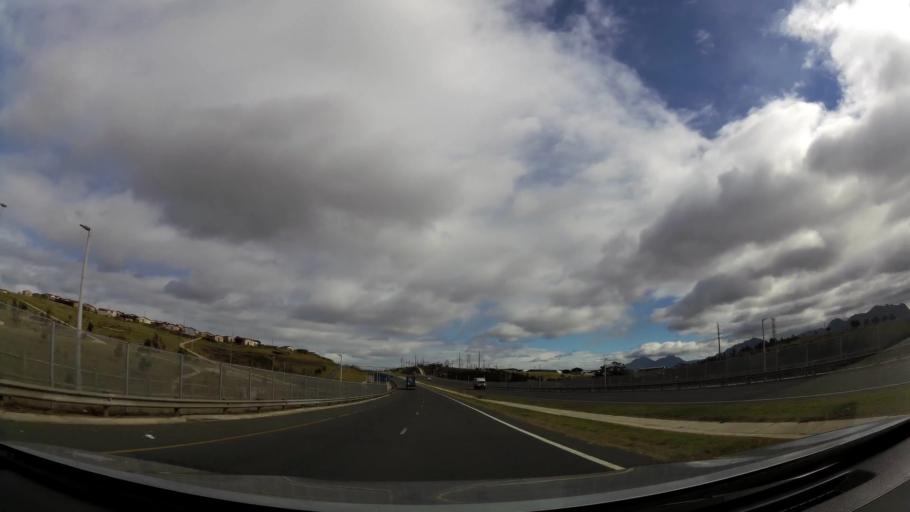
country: ZA
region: Western Cape
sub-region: Eden District Municipality
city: George
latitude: -33.9957
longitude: 22.4624
